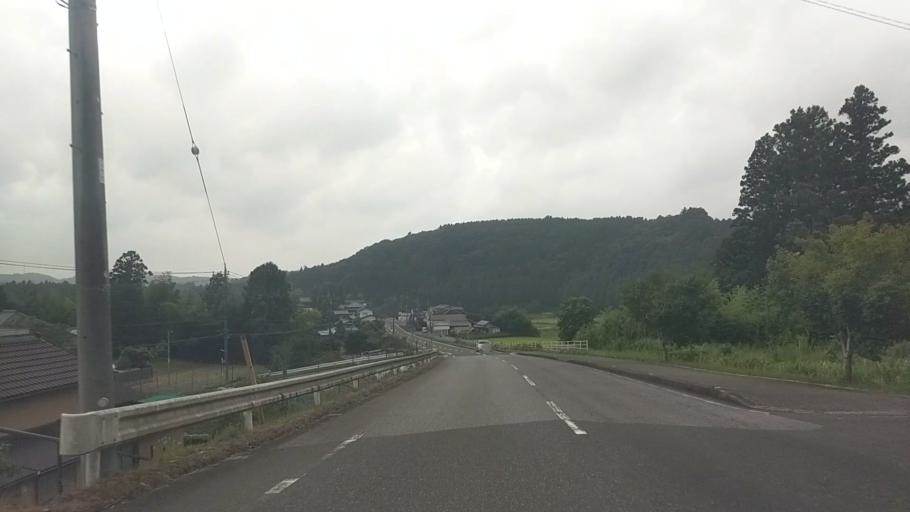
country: JP
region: Chiba
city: Kawaguchi
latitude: 35.2295
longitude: 140.1091
